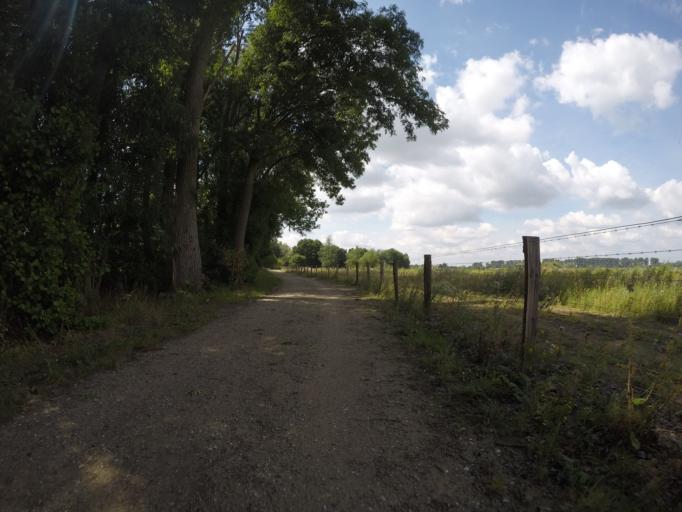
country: DE
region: North Rhine-Westphalia
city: Rees
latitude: 51.7669
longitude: 6.4445
